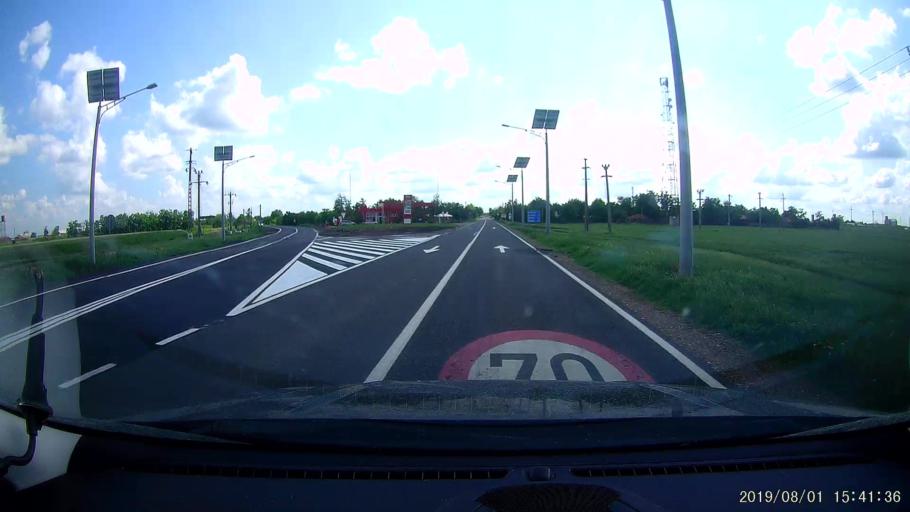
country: RO
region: Braila
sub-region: Comuna Baraganul
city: Baraganul
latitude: 44.8207
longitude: 27.5240
